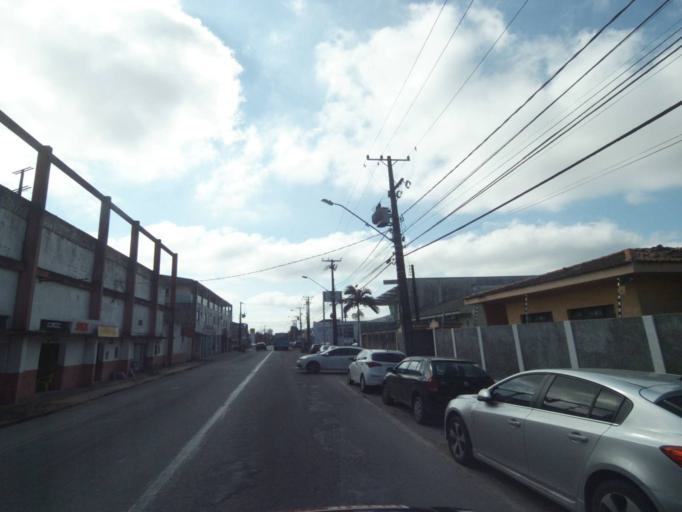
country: BR
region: Parana
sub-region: Paranagua
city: Paranagua
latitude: -25.5279
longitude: -48.5177
